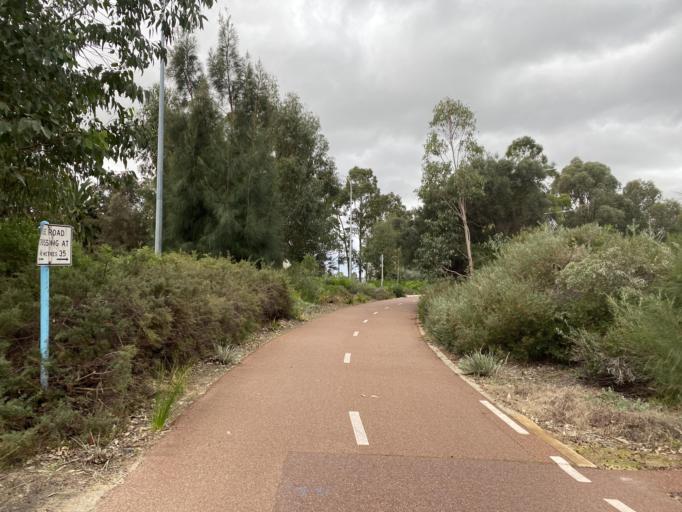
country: AU
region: Western Australia
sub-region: City of Perth
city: East Perth
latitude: -31.9636
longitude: 115.8780
